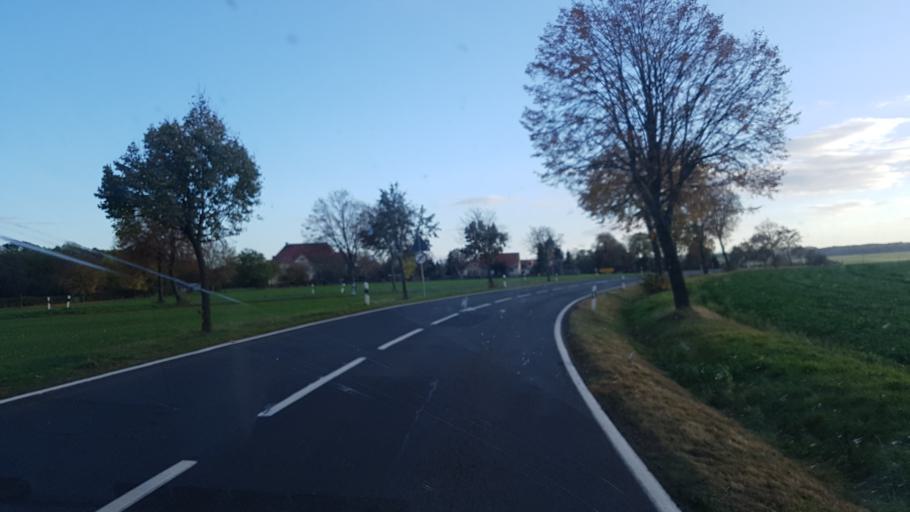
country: DE
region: Saxony
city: Dahlen
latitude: 51.3431
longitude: 13.0307
